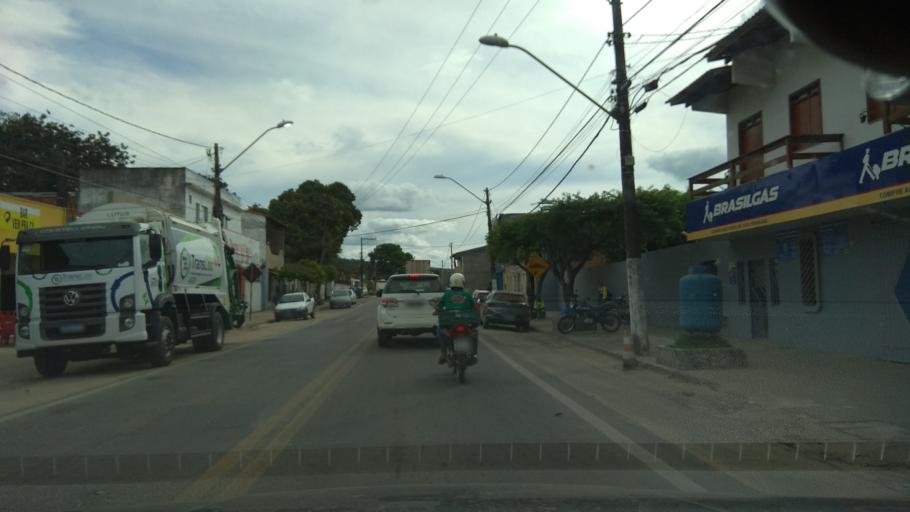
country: BR
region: Bahia
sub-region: Ipiau
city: Ipiau
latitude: -14.1345
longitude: -39.7483
